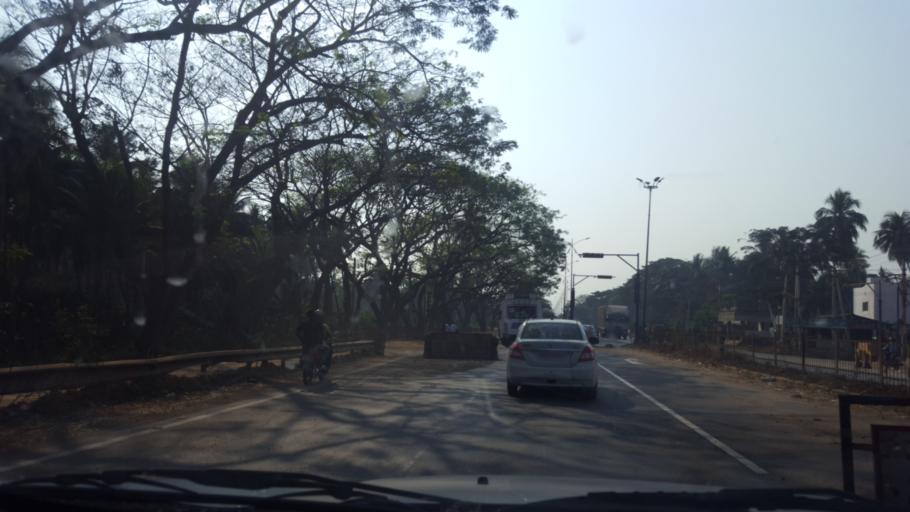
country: IN
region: Andhra Pradesh
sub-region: Vishakhapatnam
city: Anakapalle
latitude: 17.6759
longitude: 83.0141
